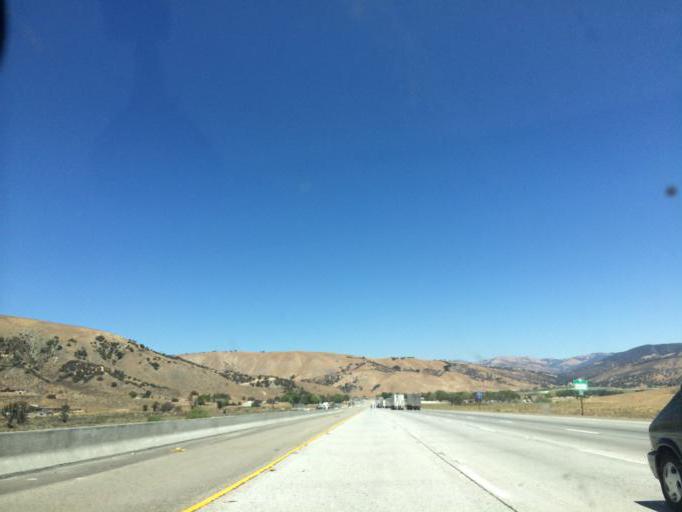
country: US
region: California
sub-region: Kern County
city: Lebec
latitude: 34.8185
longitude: -118.8805
